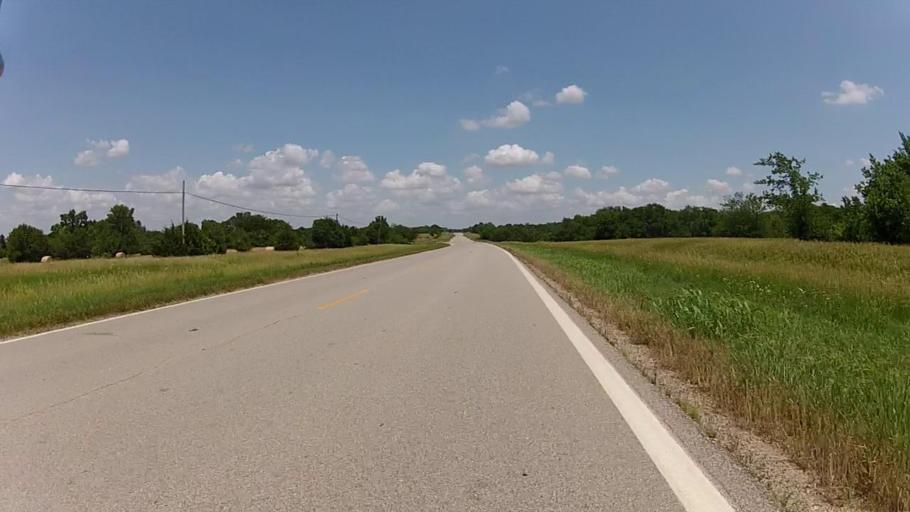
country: US
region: Kansas
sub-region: Labette County
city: Altamont
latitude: 37.1925
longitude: -95.4164
